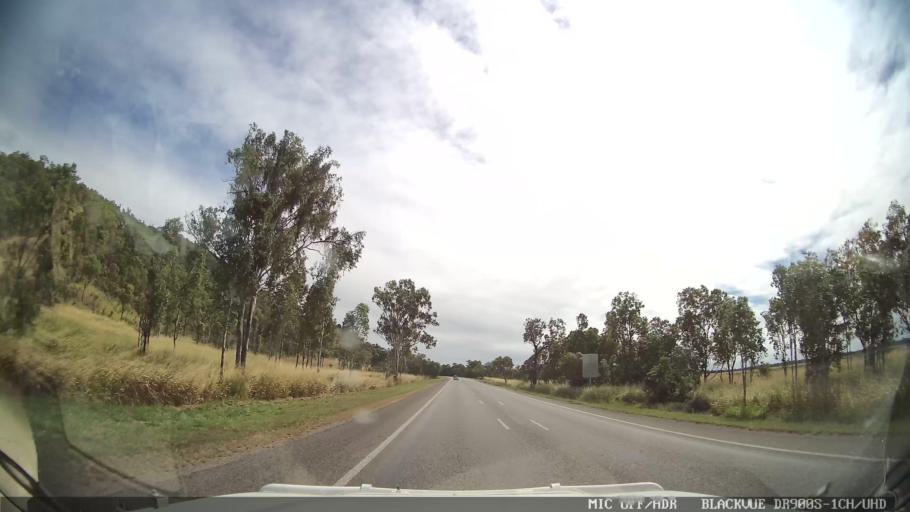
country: AU
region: Queensland
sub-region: Hinchinbrook
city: Ingham
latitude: -19.0136
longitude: 146.3652
